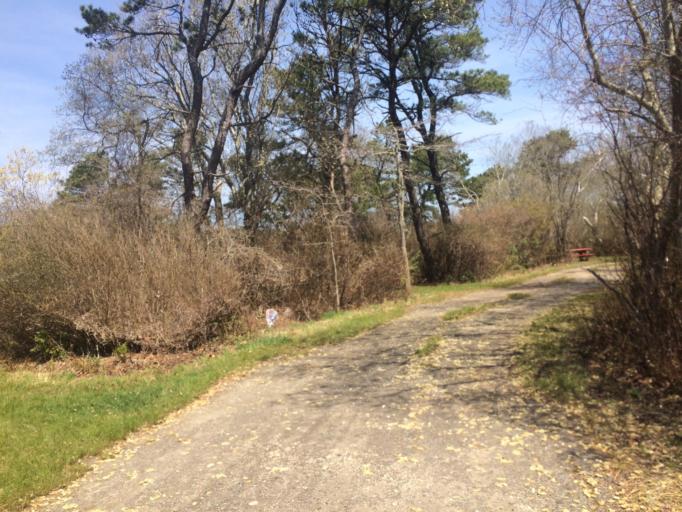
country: US
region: Massachusetts
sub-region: Barnstable County
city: Provincetown
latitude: 42.0475
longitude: -70.2016
